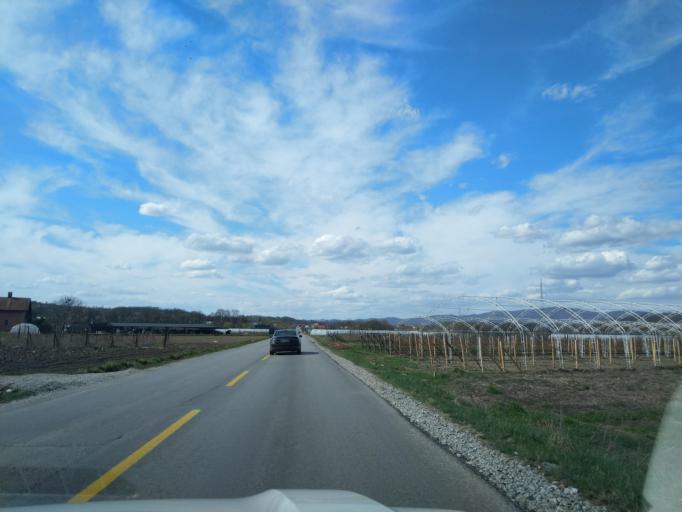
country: RS
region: Central Serbia
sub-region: Zlatiborski Okrug
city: Arilje
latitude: 43.7872
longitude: 20.1073
